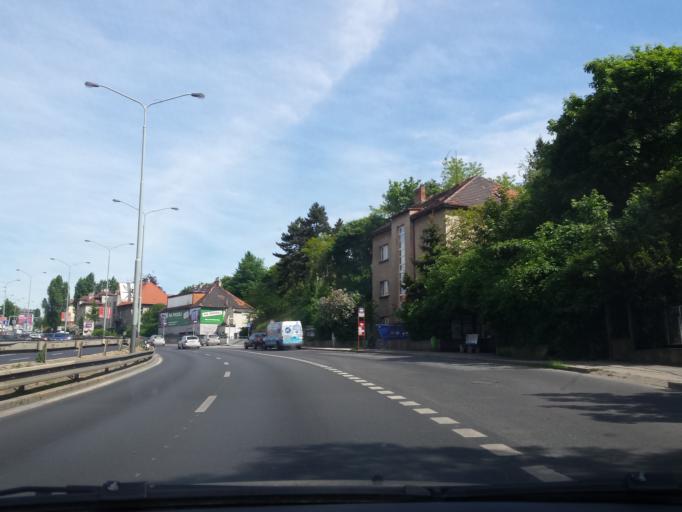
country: CZ
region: Praha
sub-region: Praha 8
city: Liben
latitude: 50.1173
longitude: 14.4572
